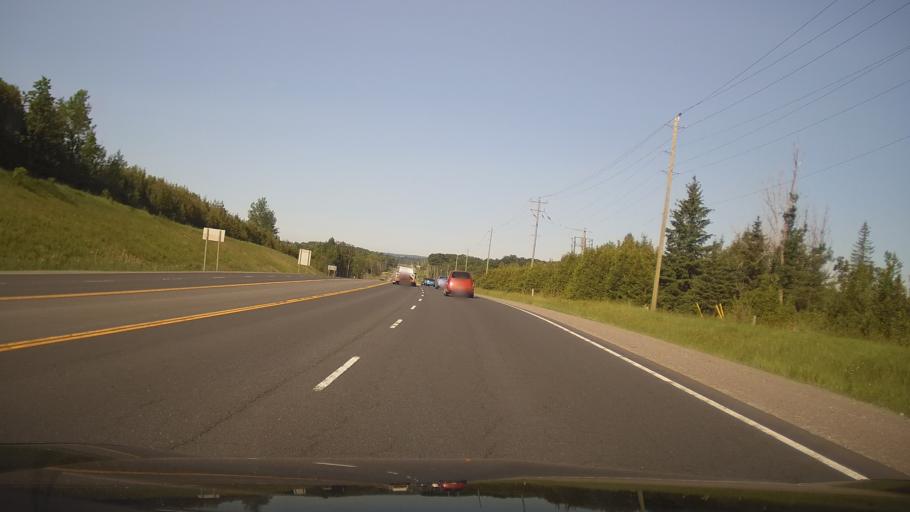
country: CA
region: Ontario
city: Peterborough
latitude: 44.3167
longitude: -78.2068
